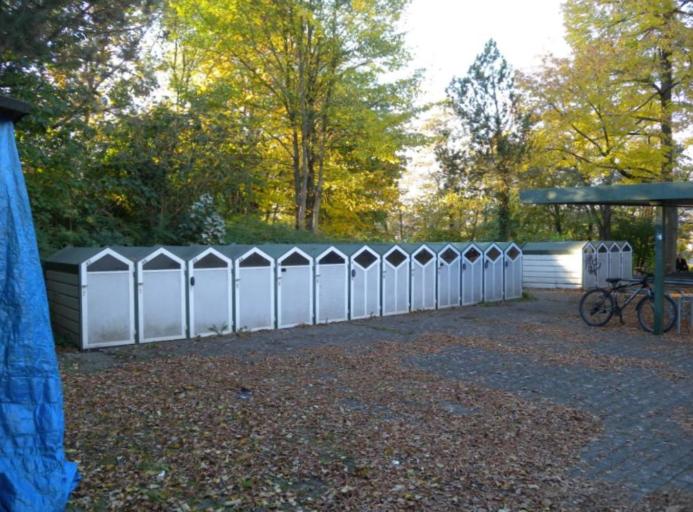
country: DE
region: Baden-Wuerttemberg
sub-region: Regierungsbezirk Stuttgart
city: Backnang
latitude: 48.9422
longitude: 9.4275
